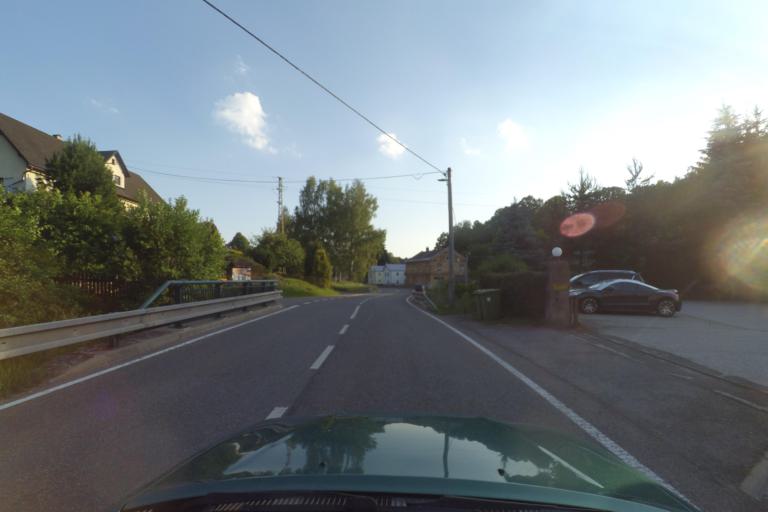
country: CZ
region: Kralovehradecky
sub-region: Okres Trutnov
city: Rudnik
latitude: 50.5949
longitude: 15.7331
